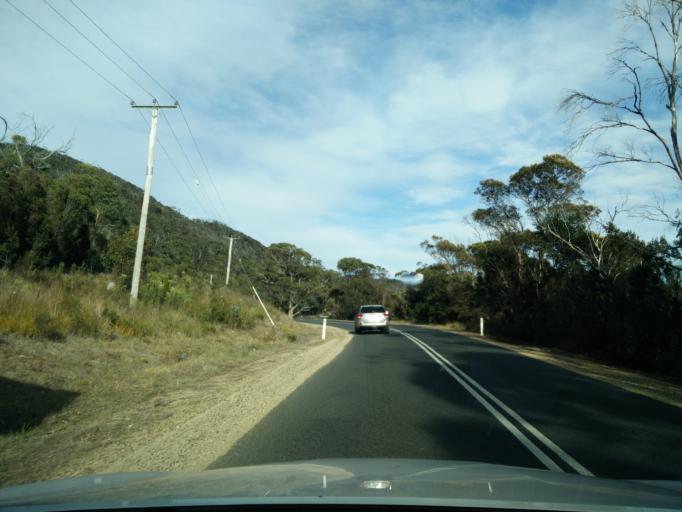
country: AU
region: Tasmania
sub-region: Break O'Day
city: St Helens
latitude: -41.8555
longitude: 148.2691
